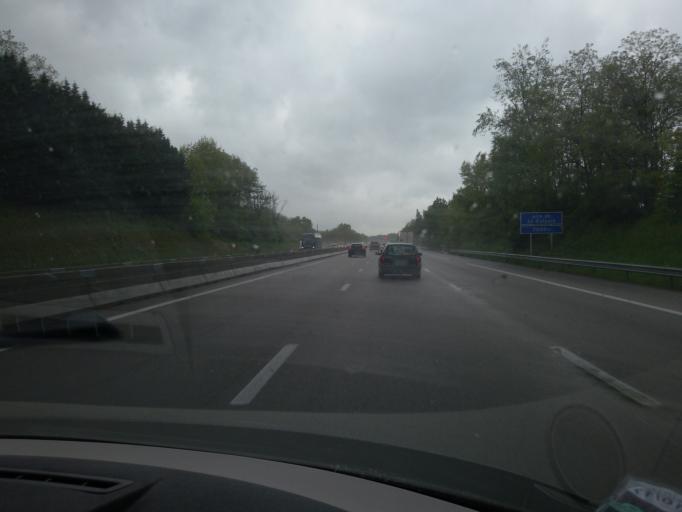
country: FR
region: Rhone-Alpes
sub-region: Departement de la Drome
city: Saint-Barthelemy-de-Vals
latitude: 45.1295
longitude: 4.8956
